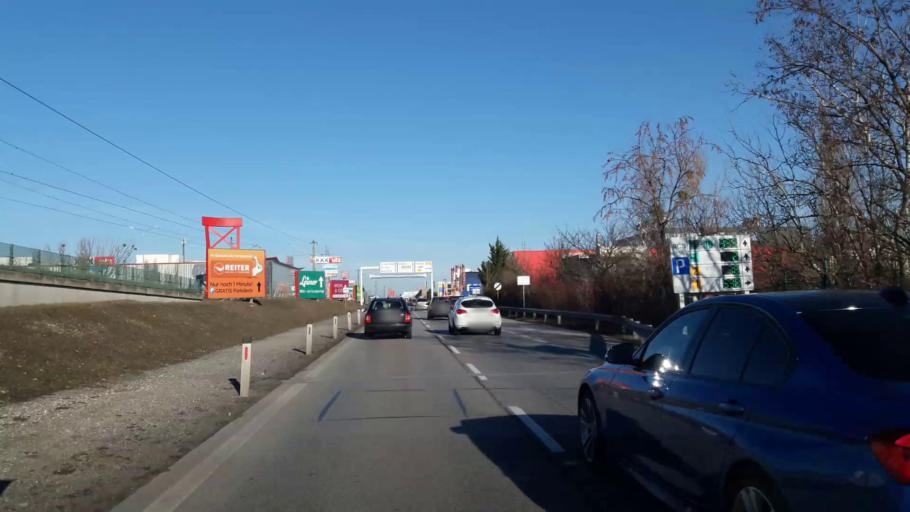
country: AT
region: Lower Austria
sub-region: Politischer Bezirk Modling
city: Wiener Neudorf
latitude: 48.1024
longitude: 16.3152
